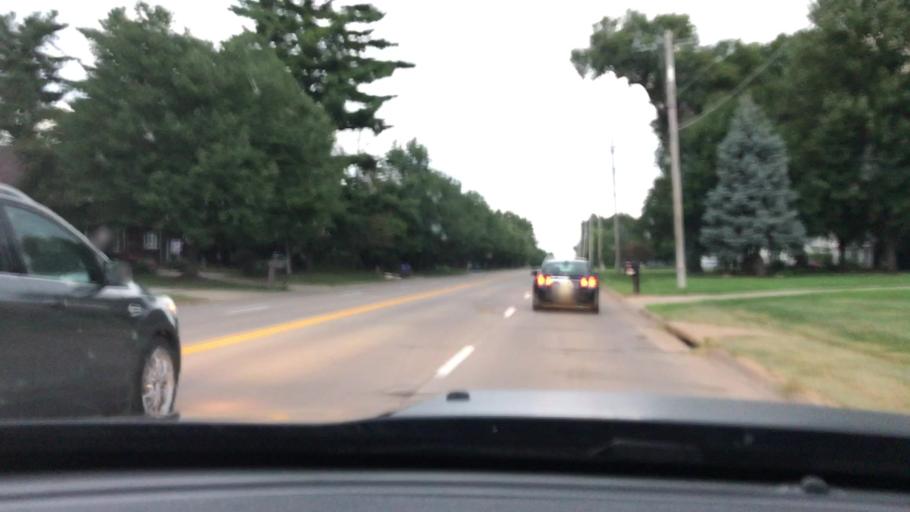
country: US
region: Iowa
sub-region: Scott County
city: Bettendorf
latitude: 41.5595
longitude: -90.5416
